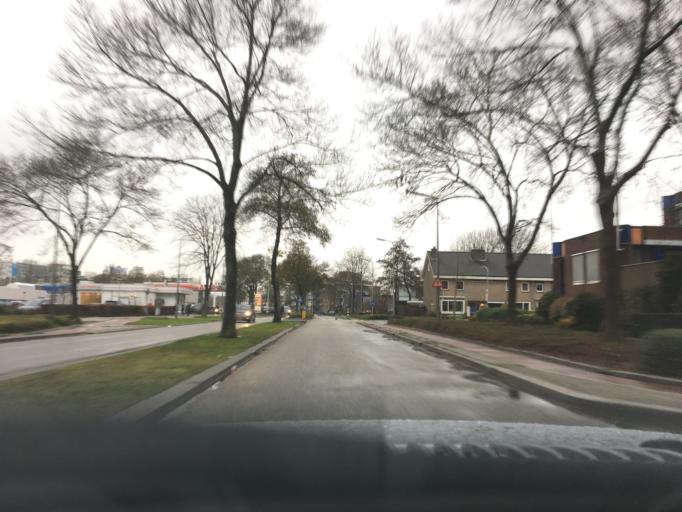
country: NL
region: South Holland
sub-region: Gemeente Dordrecht
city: Dordrecht
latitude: 51.8229
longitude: 4.6552
